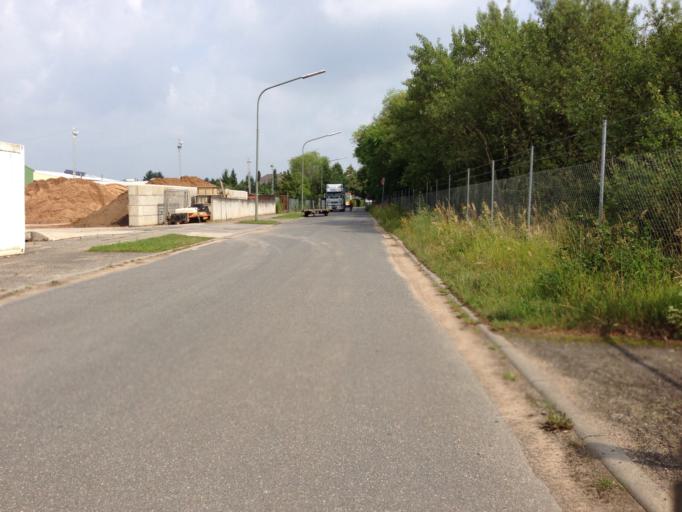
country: DE
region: Hesse
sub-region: Regierungsbezirk Darmstadt
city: Hanau am Main
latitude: 50.0955
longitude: 8.9377
